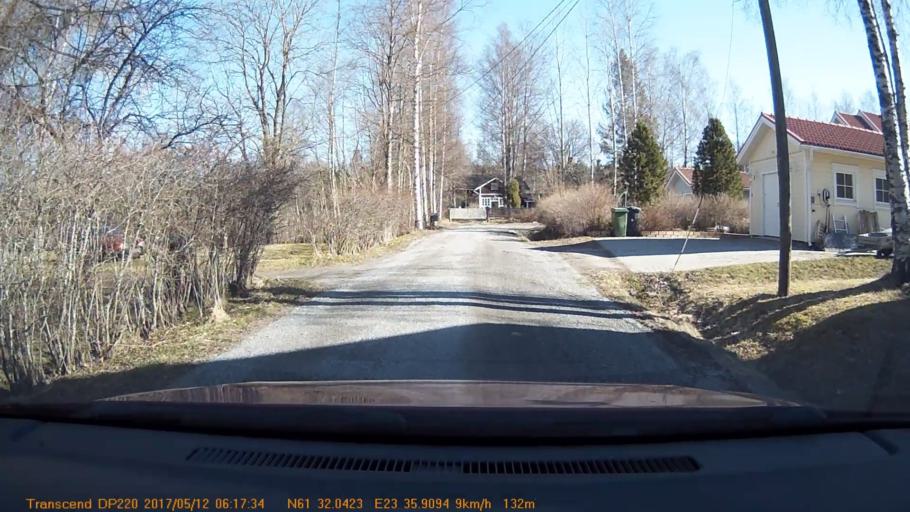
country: FI
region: Pirkanmaa
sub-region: Tampere
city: Yloejaervi
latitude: 61.5340
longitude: 23.5985
